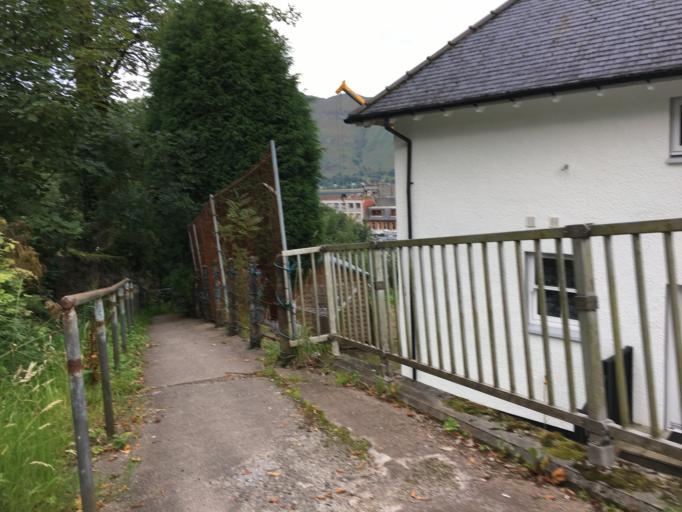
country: GB
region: Scotland
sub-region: Highland
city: Fort William
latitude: 56.8174
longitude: -5.1095
